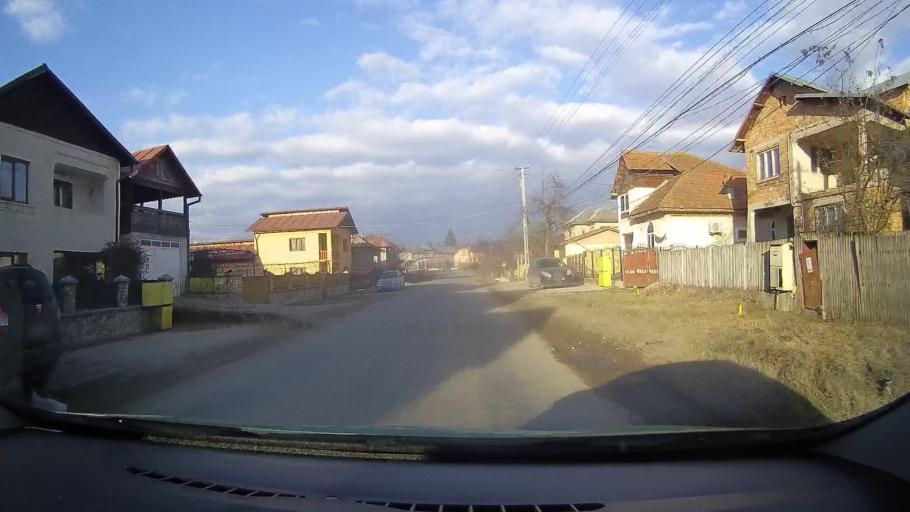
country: RO
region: Dambovita
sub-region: Comuna Ocnita
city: Ocnita
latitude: 44.9724
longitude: 25.5553
